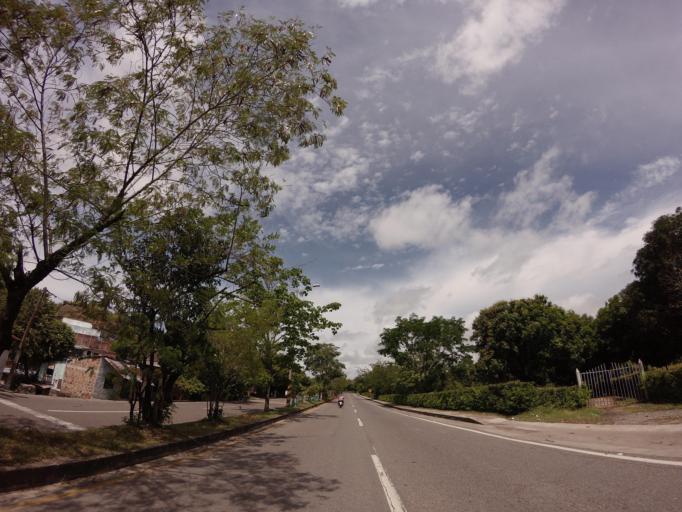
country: CO
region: Caldas
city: La Dorada
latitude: 5.4583
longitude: -74.6722
